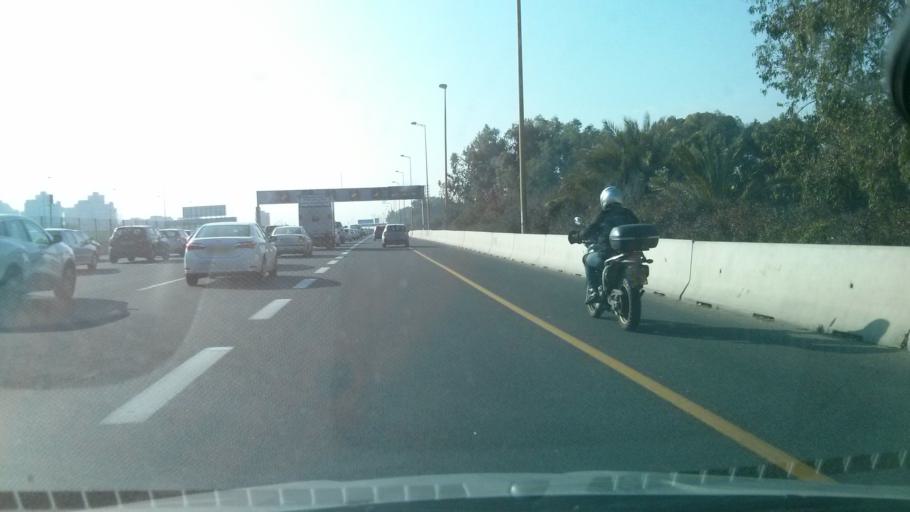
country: IL
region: Tel Aviv
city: Ramat HaSharon
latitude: 32.1324
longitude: 34.8097
